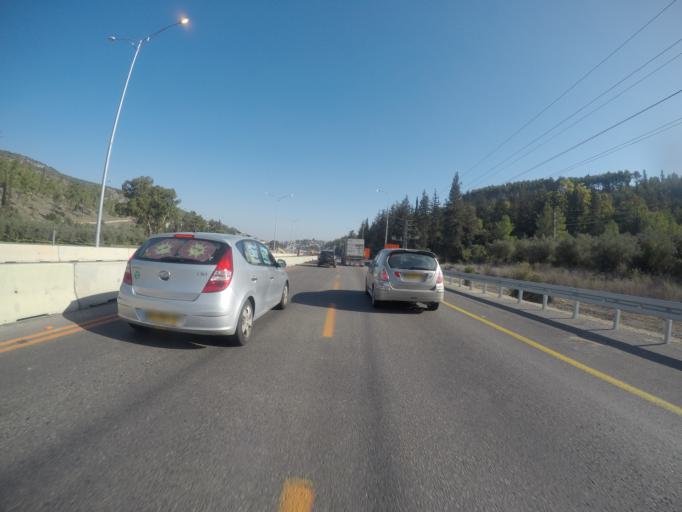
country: IL
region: Haifa
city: Daliyat el Karmil
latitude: 32.6528
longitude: 35.0933
